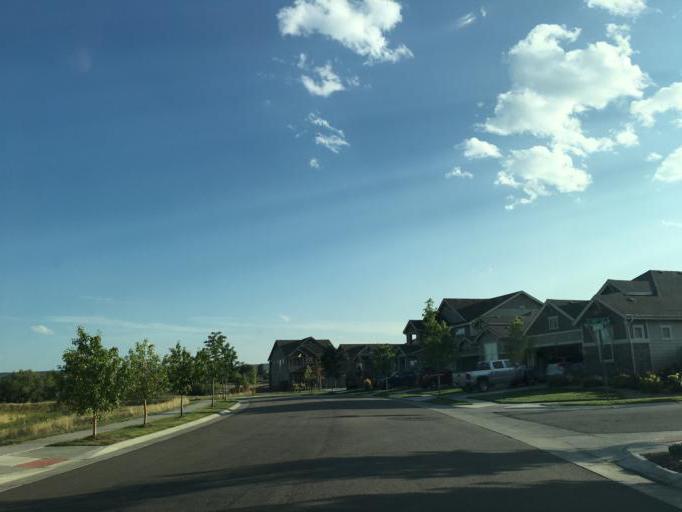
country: US
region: Colorado
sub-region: Jefferson County
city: Applewood
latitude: 39.7871
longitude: -105.1696
